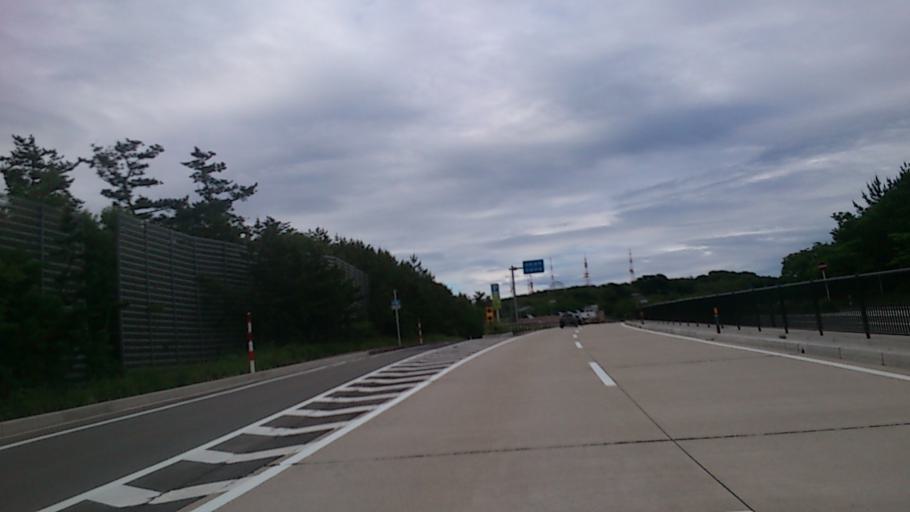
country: JP
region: Akita
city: Akita Shi
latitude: 39.6823
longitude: 140.0737
